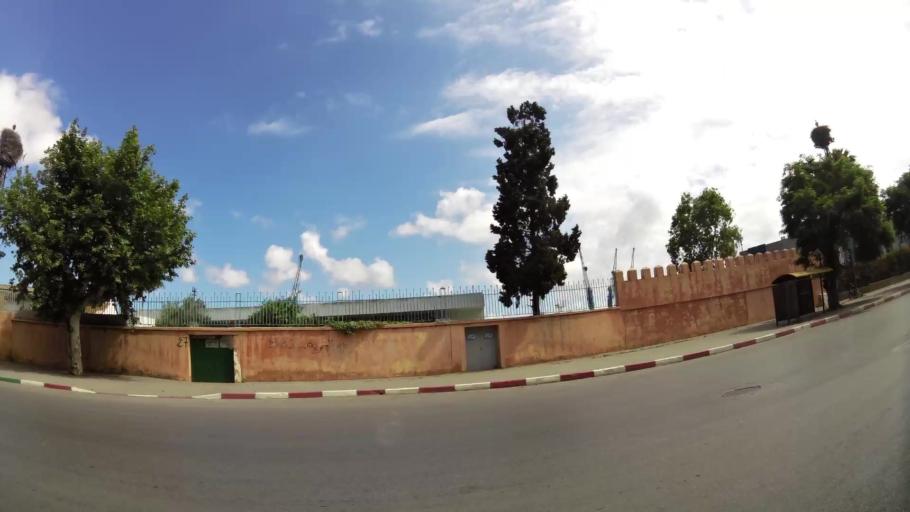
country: MA
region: Gharb-Chrarda-Beni Hssen
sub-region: Kenitra Province
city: Kenitra
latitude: 34.2648
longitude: -6.5815
